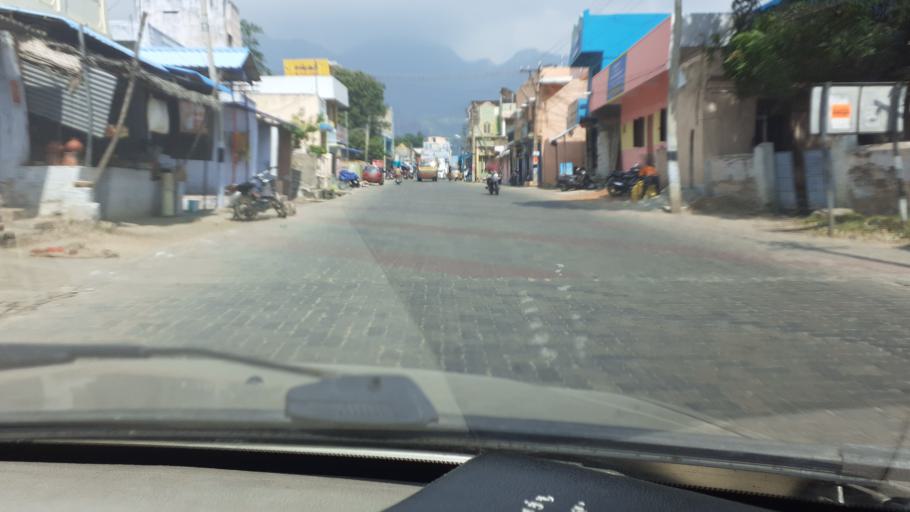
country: IN
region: Tamil Nadu
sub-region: Kanniyakumari
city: Suchindram
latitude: 8.2485
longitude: 77.5212
